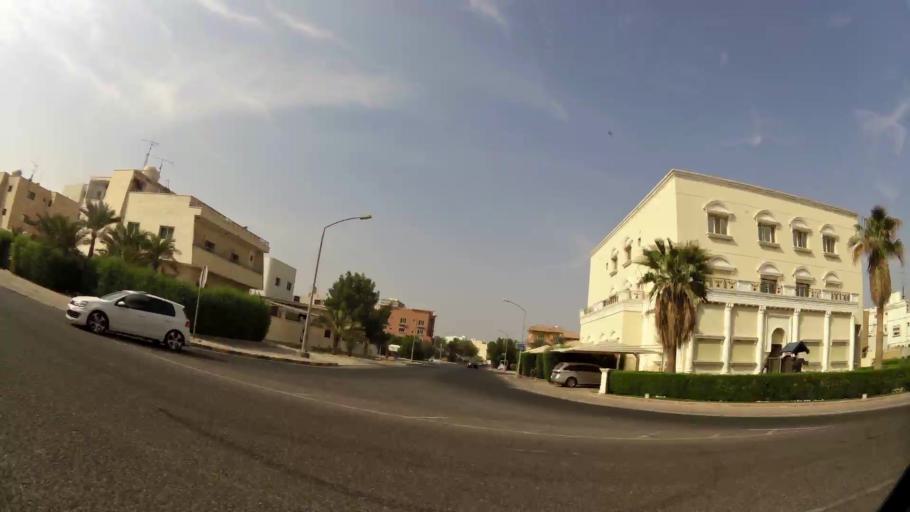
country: KW
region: Al Asimah
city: Ash Shamiyah
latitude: 29.3241
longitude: 47.9597
